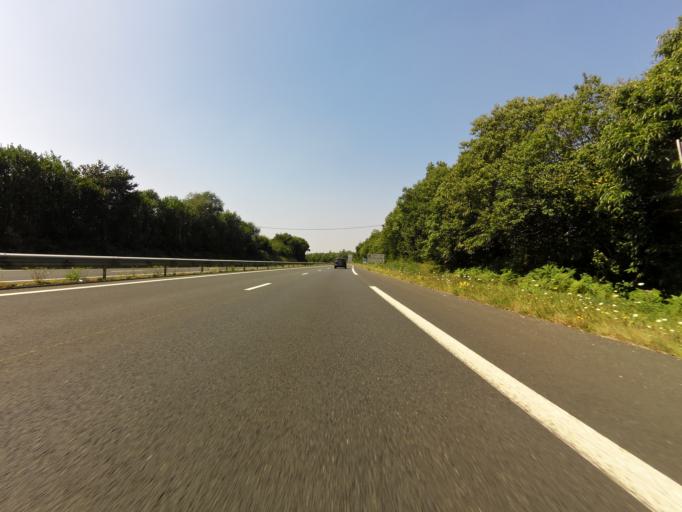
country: FR
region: Brittany
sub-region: Departement du Finistere
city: Plomelin
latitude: 47.9603
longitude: -4.1596
